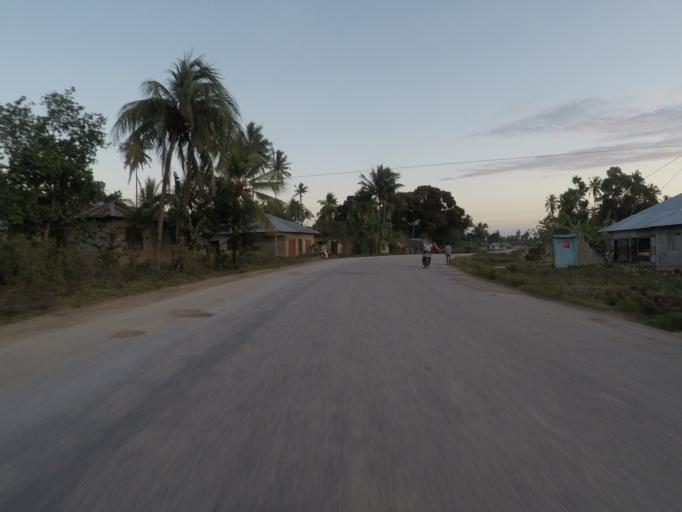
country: TZ
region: Zanzibar North
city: Gamba
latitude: -5.9995
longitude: 39.2520
